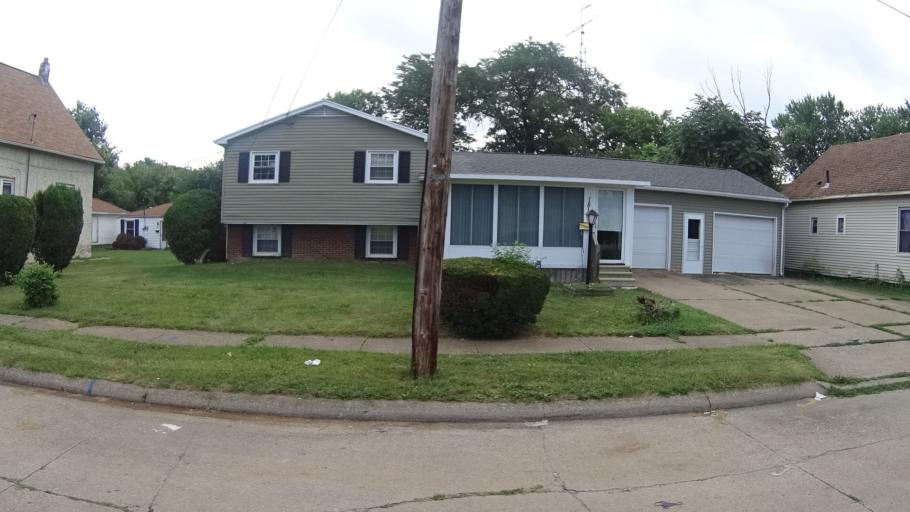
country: US
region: Ohio
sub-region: Erie County
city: Sandusky
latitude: 41.4388
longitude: -82.7235
